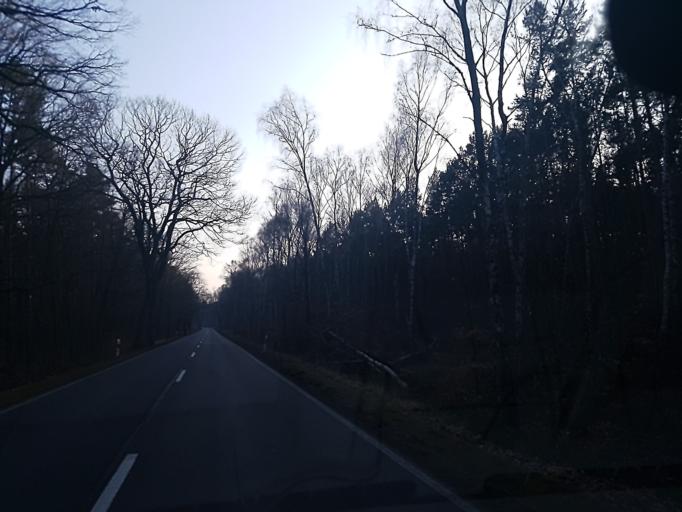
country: DE
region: Brandenburg
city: Wiesenburg
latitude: 52.0197
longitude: 12.4603
